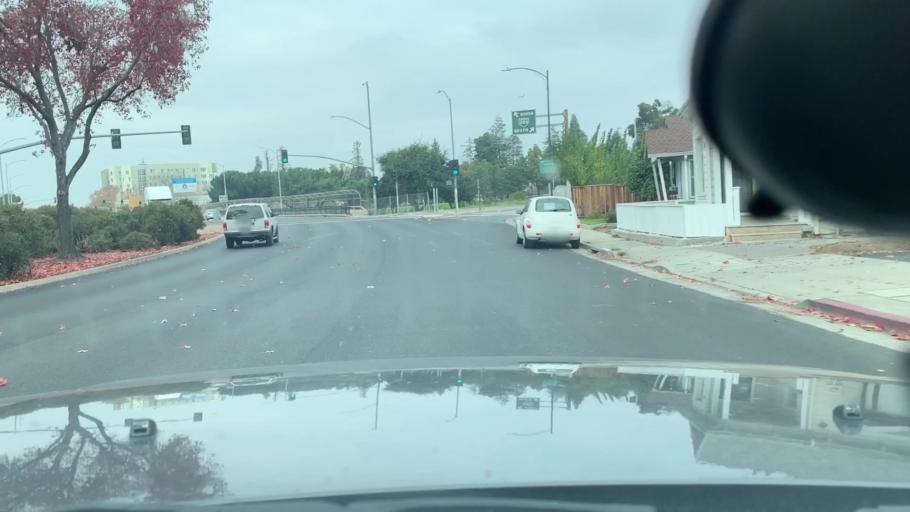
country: US
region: California
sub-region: Santa Clara County
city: San Jose
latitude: 37.3212
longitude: -121.8975
